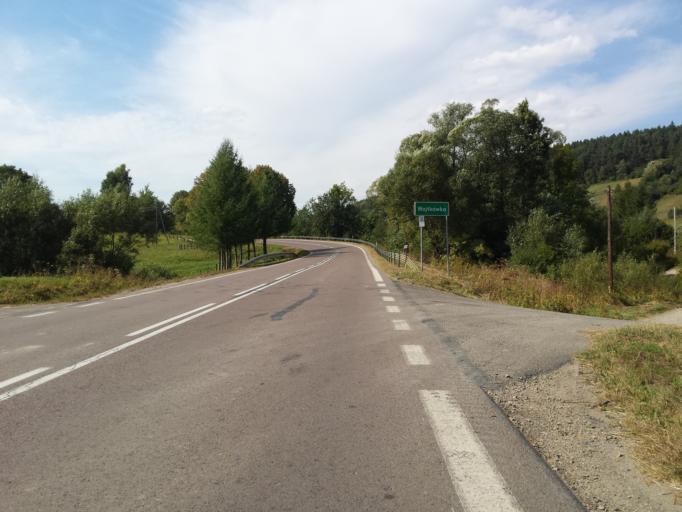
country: PL
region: Subcarpathian Voivodeship
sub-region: Powiat bieszczadzki
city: Ustrzyki Dolne
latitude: 49.5528
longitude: 22.5726
